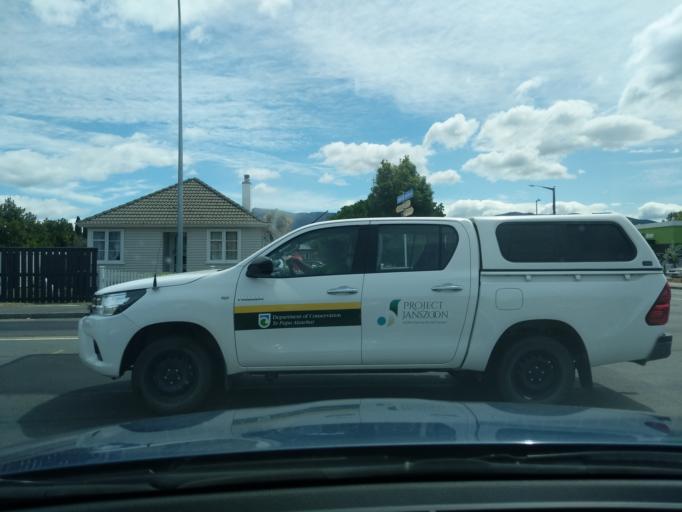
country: NZ
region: Tasman
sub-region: Tasman District
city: Motueka
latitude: -41.1156
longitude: 173.0110
